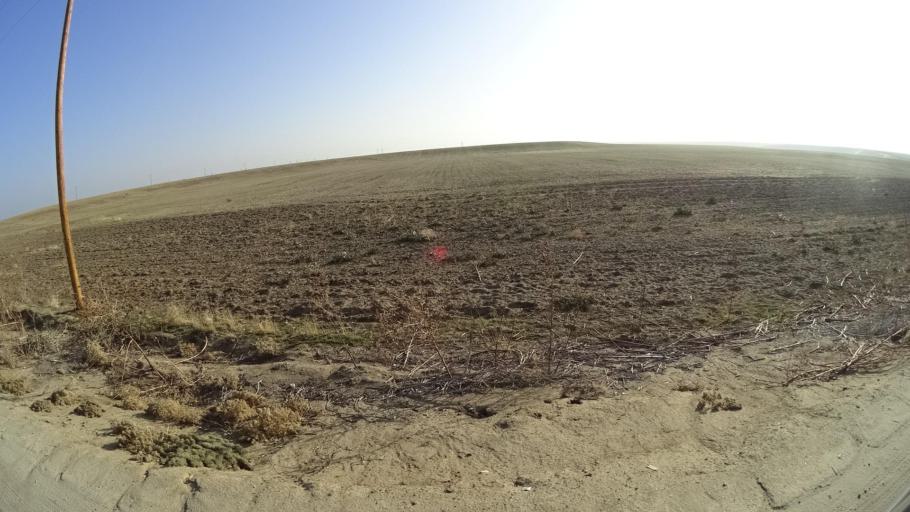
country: US
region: California
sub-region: Tulare County
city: Richgrove
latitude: 35.7738
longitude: -119.0807
